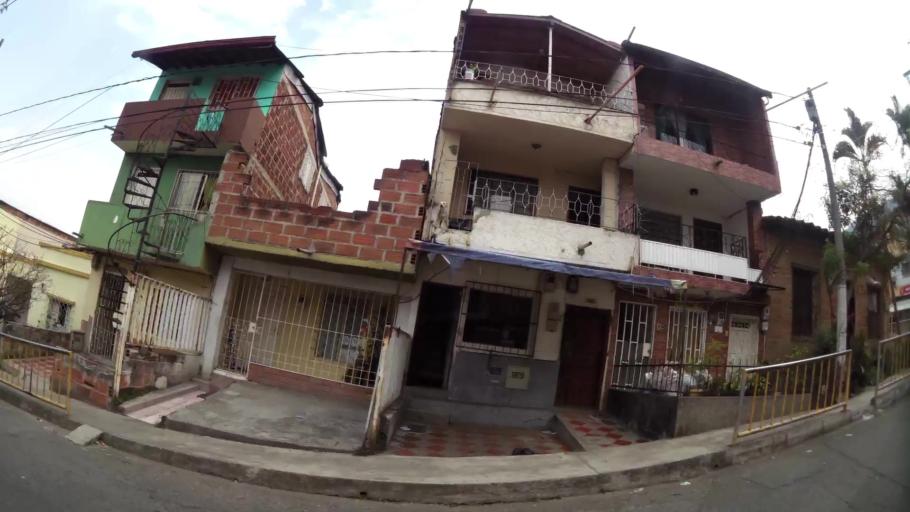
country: CO
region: Antioquia
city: Medellin
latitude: 6.2834
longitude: -75.5494
